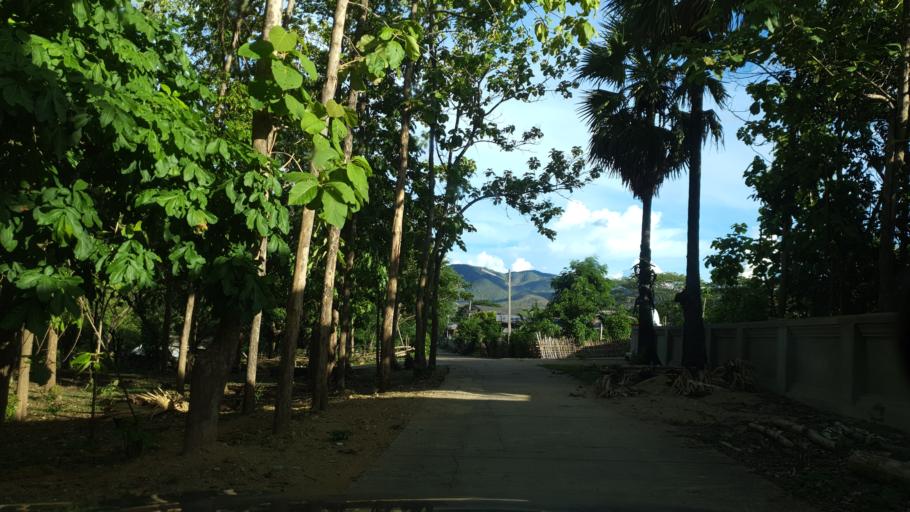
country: TH
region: Lampang
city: Sop Prap
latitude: 17.8779
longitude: 99.2979
